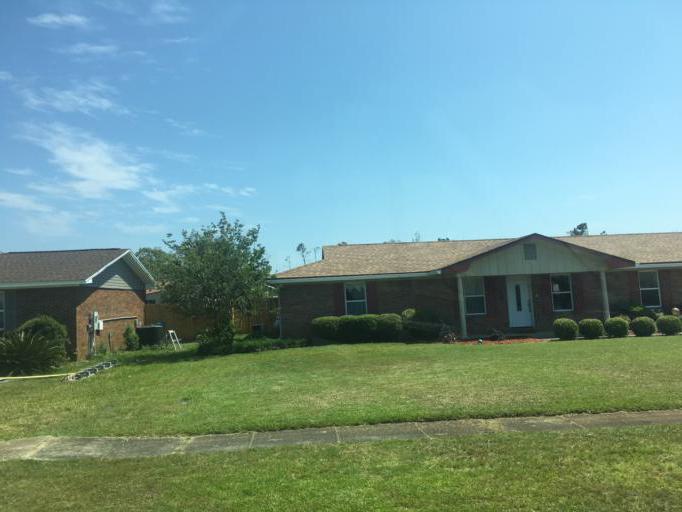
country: US
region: Florida
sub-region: Bay County
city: Lynn Haven
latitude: 30.2206
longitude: -85.6544
